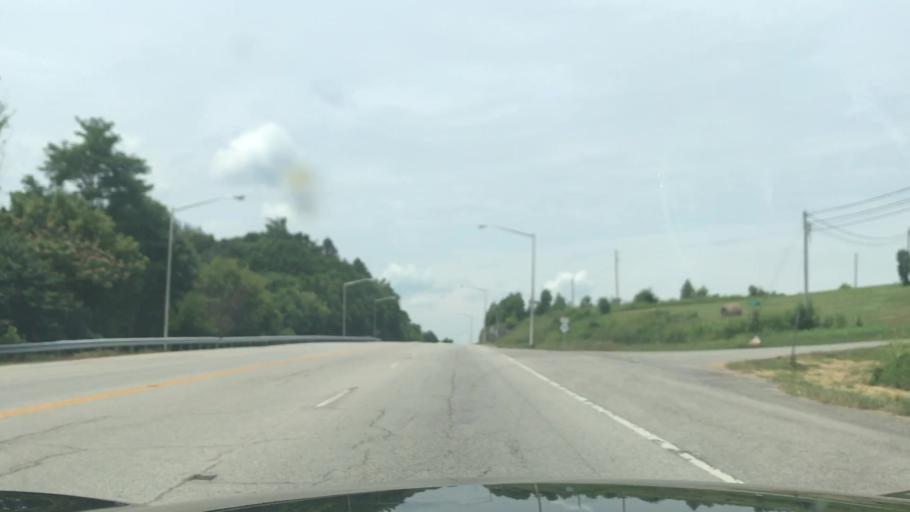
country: US
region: Kentucky
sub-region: Green County
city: Greensburg
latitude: 37.2727
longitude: -85.5011
